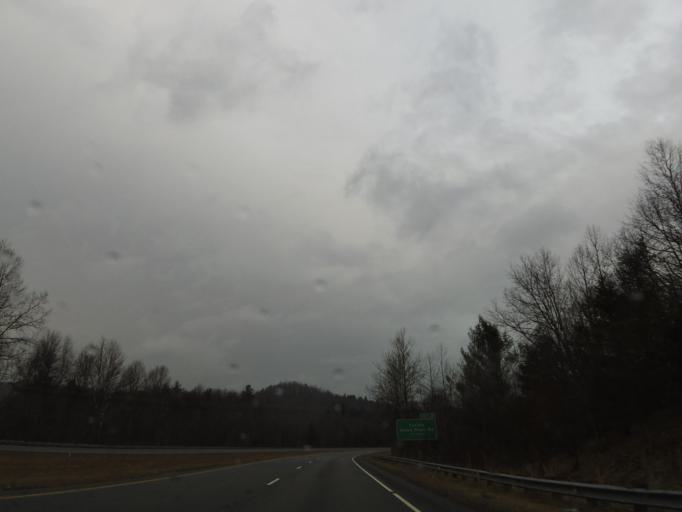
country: US
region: North Carolina
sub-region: Henderson County
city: Flat Rock
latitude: 35.2021
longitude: -82.4512
